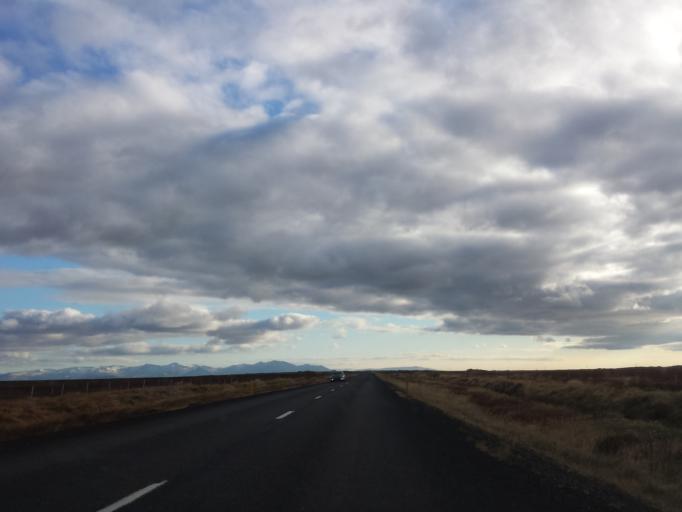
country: IS
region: West
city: Borgarnes
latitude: 64.7270
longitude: -22.1769
